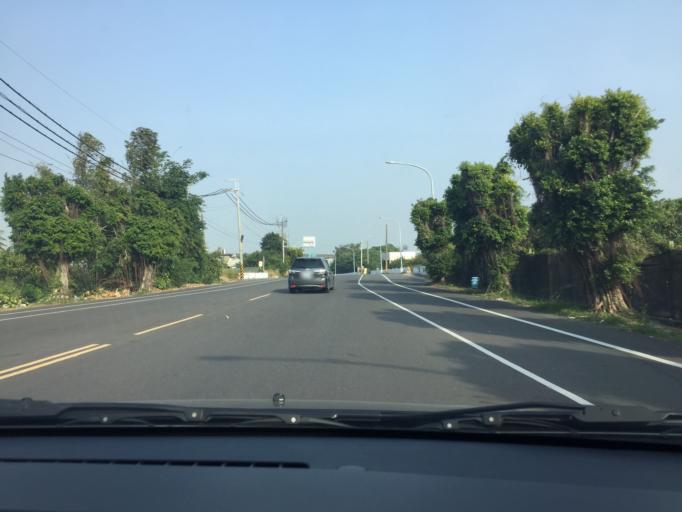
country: TW
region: Taiwan
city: Xinying
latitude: 23.1892
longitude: 120.2715
